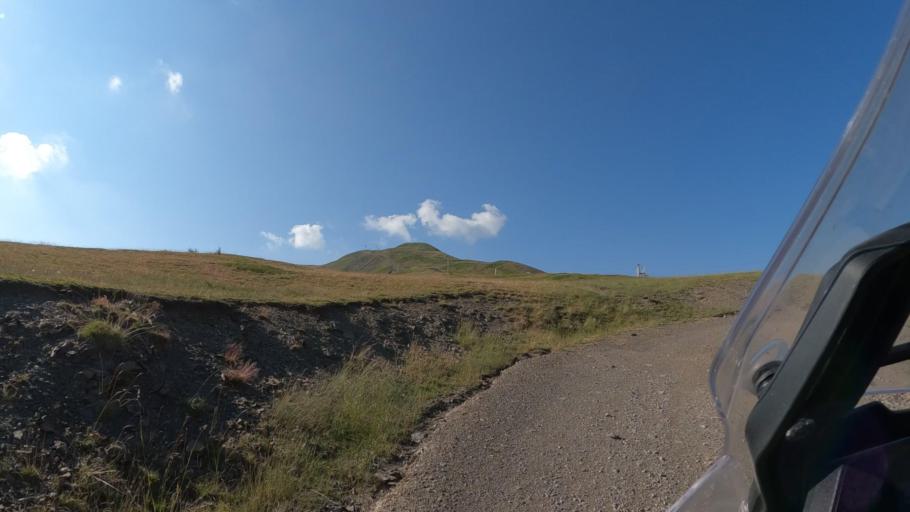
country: FR
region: Provence-Alpes-Cote d'Azur
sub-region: Departement des Hautes-Alpes
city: Guillestre
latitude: 44.6043
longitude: 6.6264
